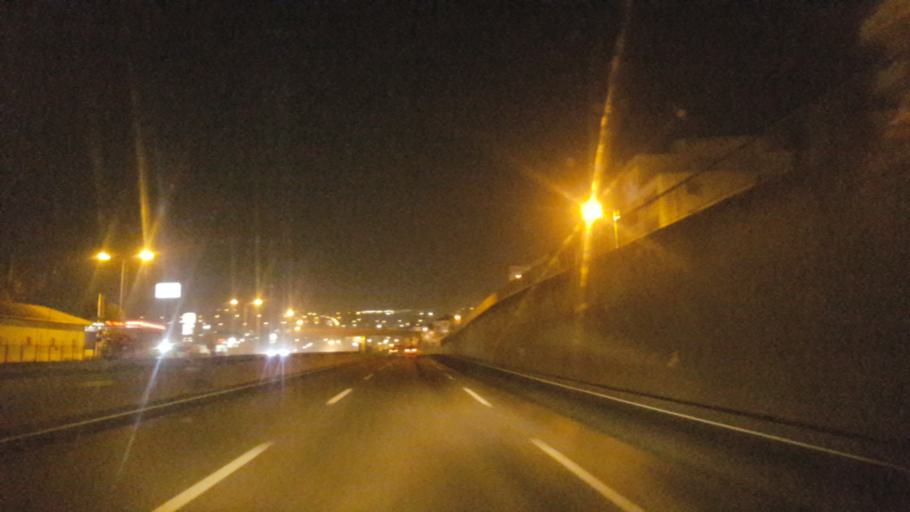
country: TR
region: Kocaeli
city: Tavsanli
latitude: 40.7861
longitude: 29.5348
